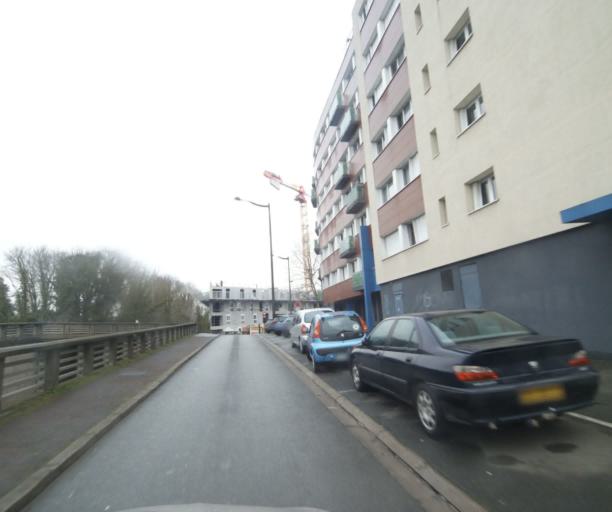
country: FR
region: Nord-Pas-de-Calais
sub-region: Departement du Nord
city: Anzin
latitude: 50.3594
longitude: 3.5166
